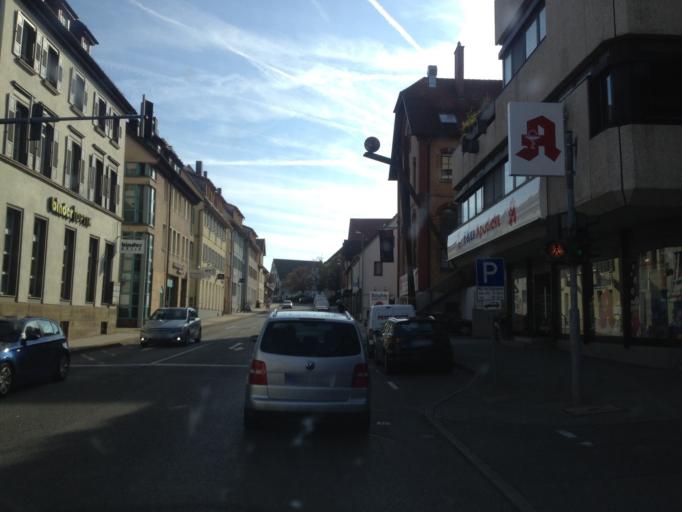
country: DE
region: Baden-Wuerttemberg
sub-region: Regierungsbezirk Stuttgart
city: Herrenberg
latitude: 48.5948
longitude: 8.8693
